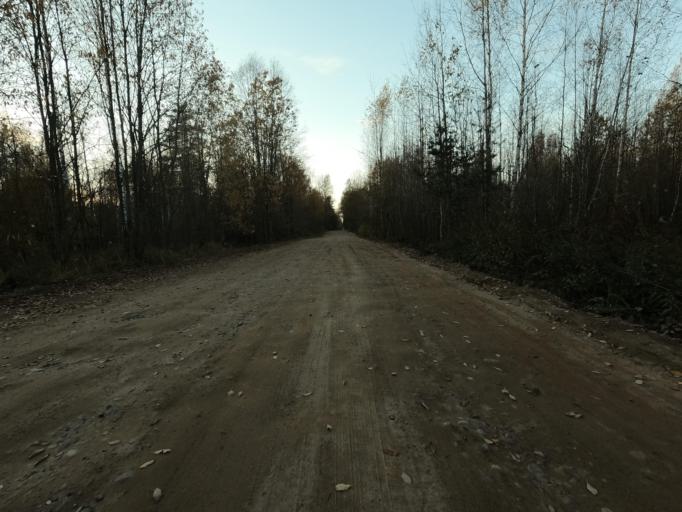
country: RU
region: Leningrad
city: Mga
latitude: 59.7570
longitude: 31.2736
